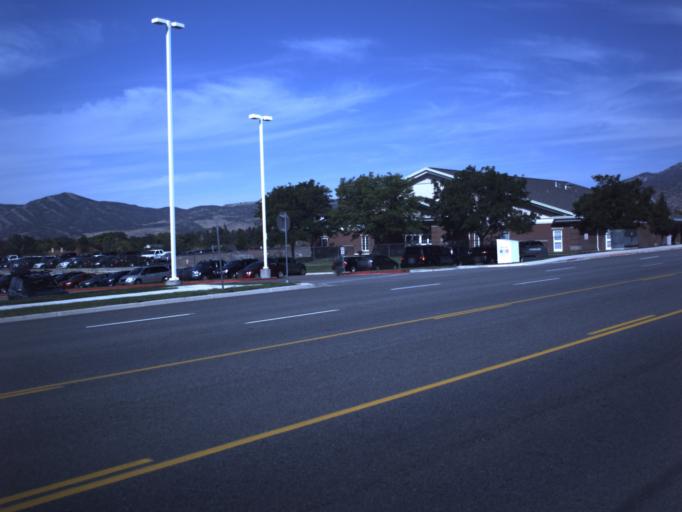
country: US
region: Utah
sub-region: Utah County
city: Cedar Hills
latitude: 40.4191
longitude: -111.7734
